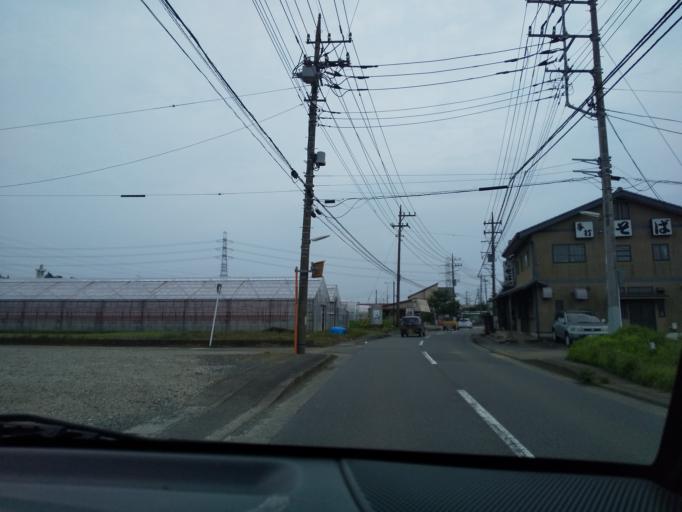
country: JP
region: Kanagawa
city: Atsugi
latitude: 35.4187
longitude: 139.3919
